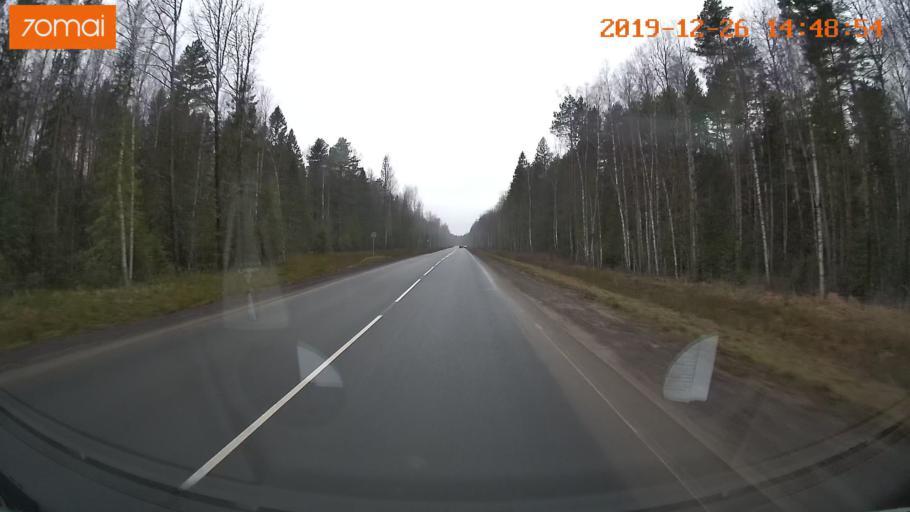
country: RU
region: Jaroslavl
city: Poshekhon'ye
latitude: 58.3417
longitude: 38.9608
